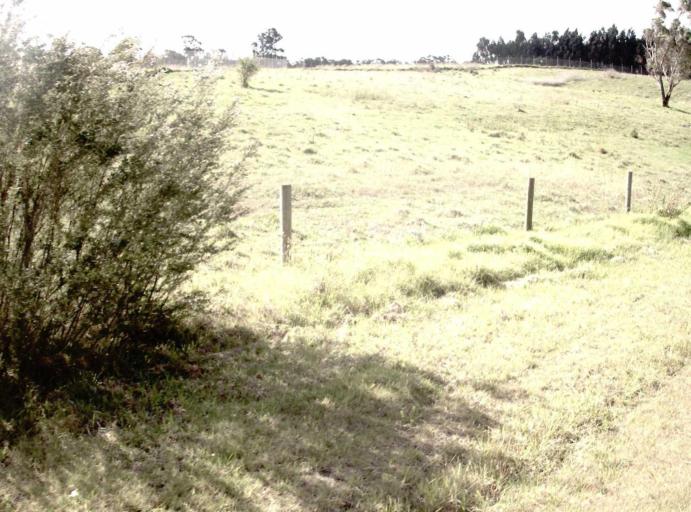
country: AU
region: Victoria
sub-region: Latrobe
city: Morwell
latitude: -38.2033
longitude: 146.4012
